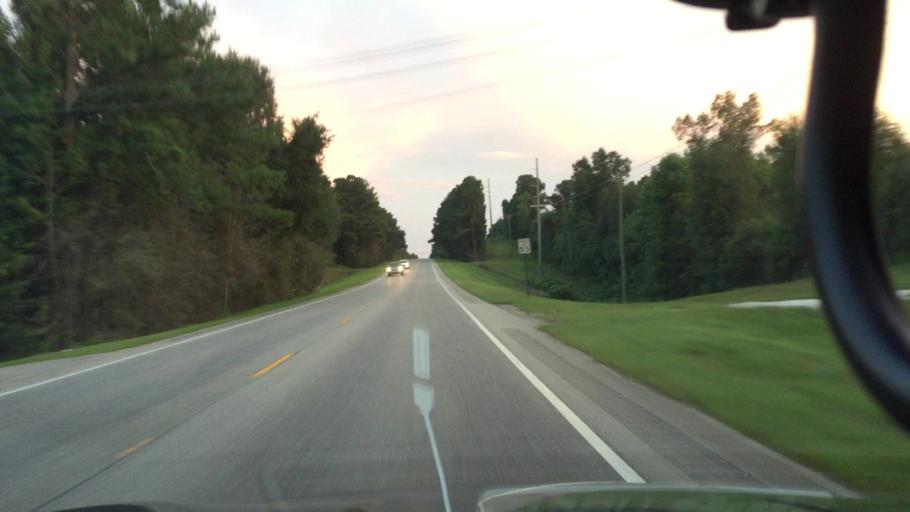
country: US
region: Alabama
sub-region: Coffee County
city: Enterprise
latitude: 31.3713
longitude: -85.8700
